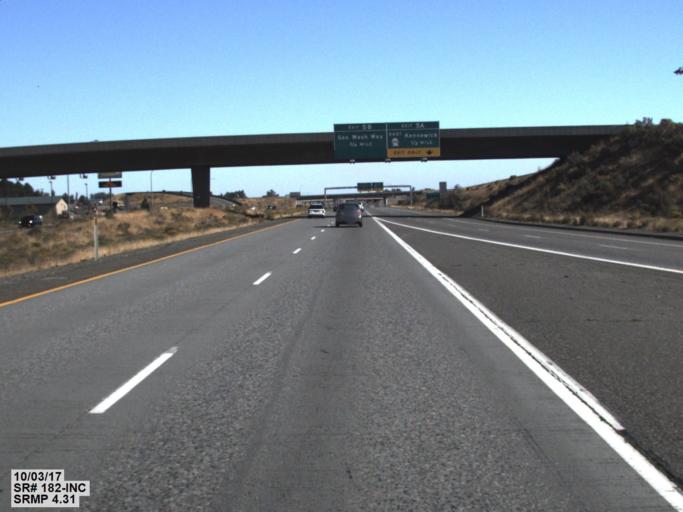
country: US
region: Washington
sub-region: Benton County
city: Richland
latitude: 46.2587
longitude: -119.2761
